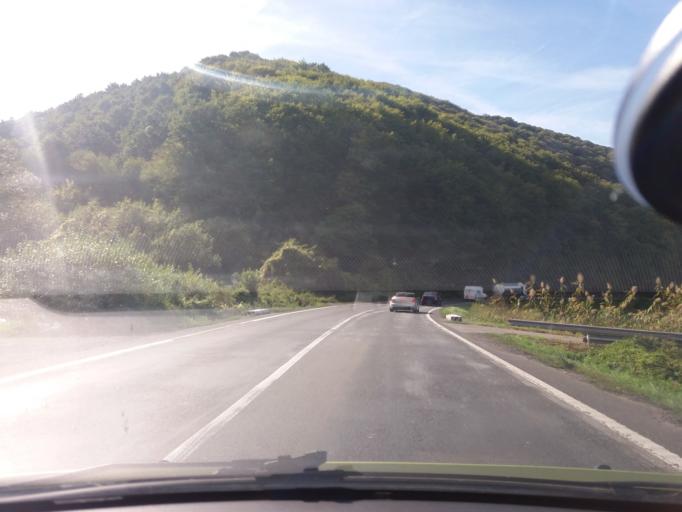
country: RO
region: Hunedoara
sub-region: Comuna Ilia
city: Ilia
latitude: 45.9205
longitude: 22.7046
